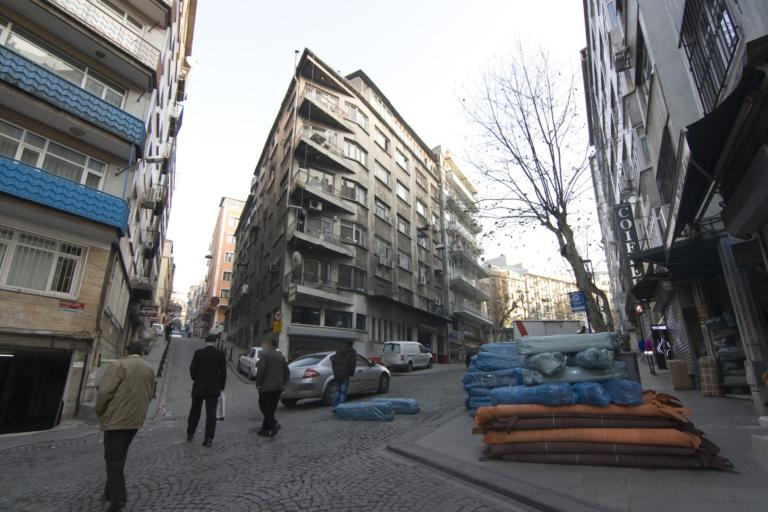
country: TR
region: Istanbul
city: Eminoenue
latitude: 41.0064
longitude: 28.9702
